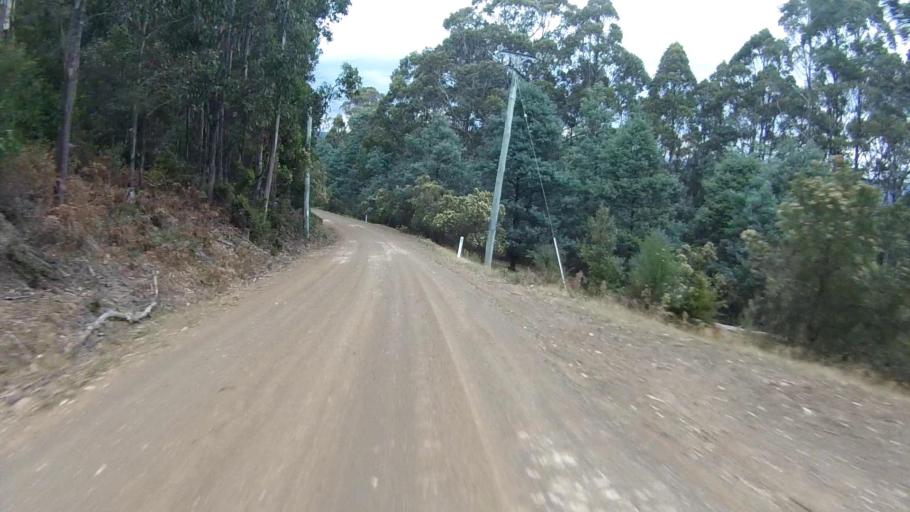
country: AU
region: Tasmania
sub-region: Huon Valley
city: Huonville
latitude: -42.9545
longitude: 147.0466
